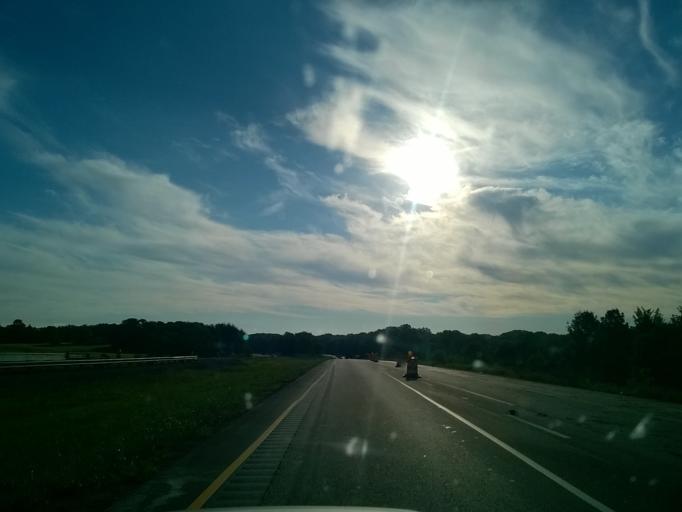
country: US
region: Indiana
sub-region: Gibson County
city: Haubstadt
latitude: 38.1696
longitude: -87.4369
